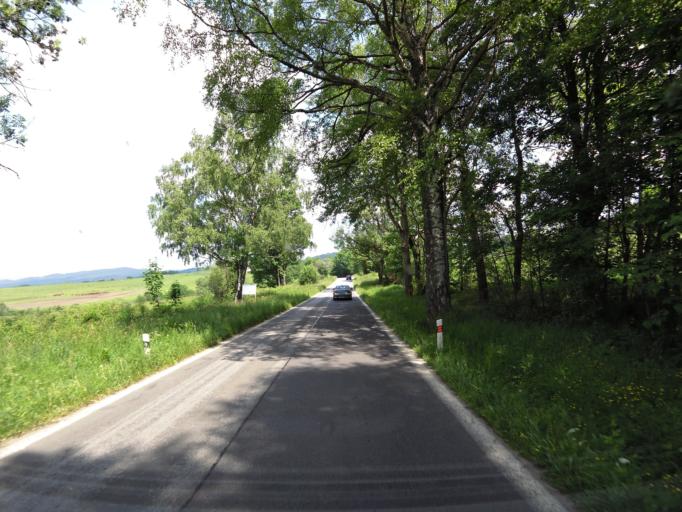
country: CZ
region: Jihocesky
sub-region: Okres Cesky Krumlov
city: Horni Plana
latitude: 48.8151
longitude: 13.9661
